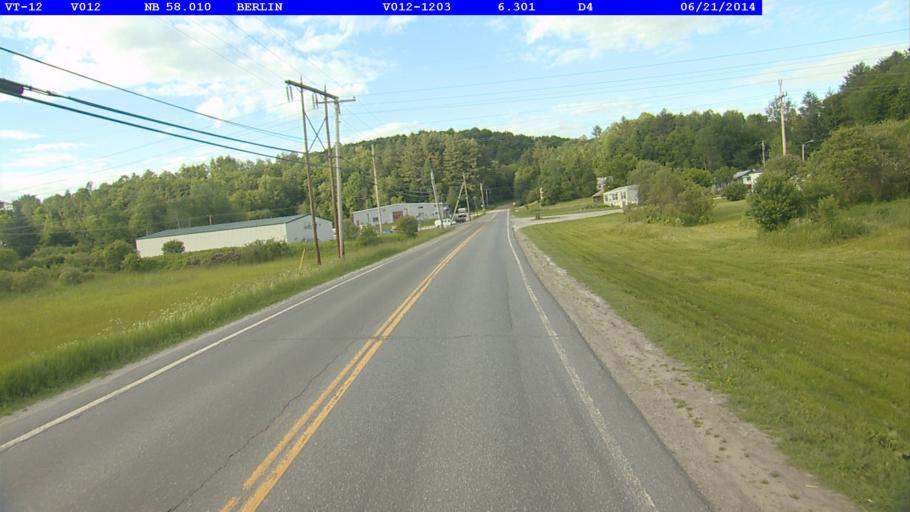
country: US
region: Vermont
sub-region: Washington County
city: Montpelier
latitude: 44.2436
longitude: -72.5943
